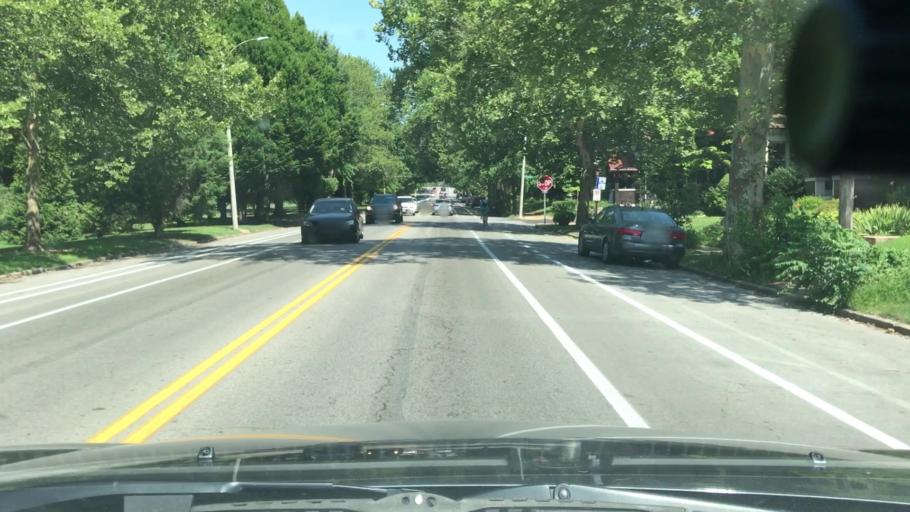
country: US
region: Missouri
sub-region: City of Saint Louis
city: St. Louis
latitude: 38.6039
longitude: -90.2531
